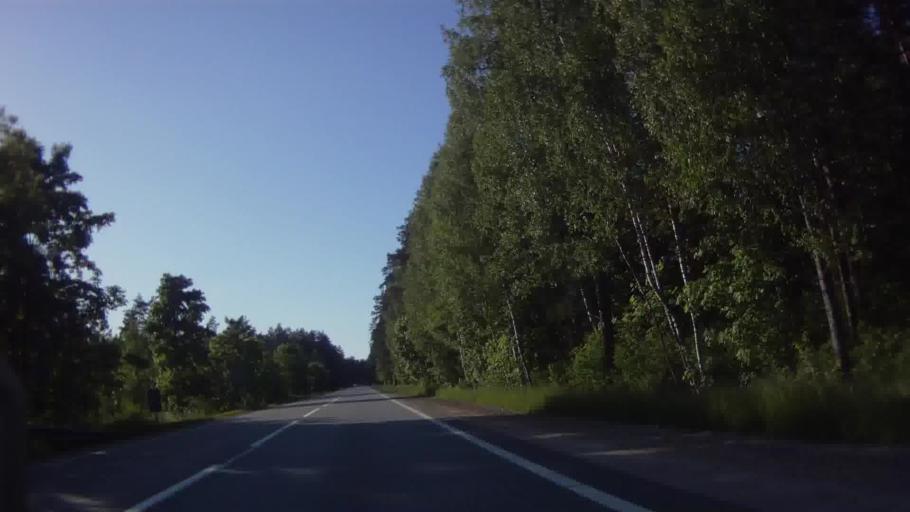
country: LV
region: Riga
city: Bergi
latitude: 56.9874
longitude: 24.3188
